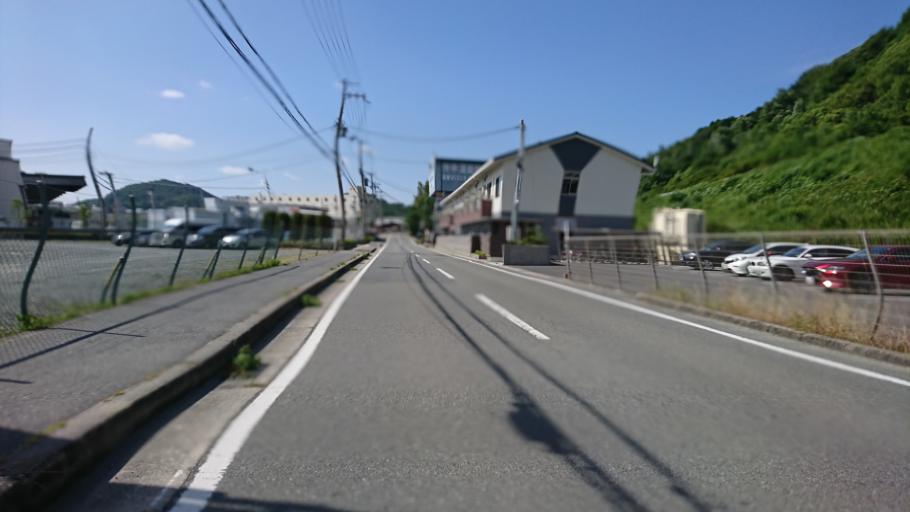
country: JP
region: Hyogo
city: Shirahamacho-usazakiminami
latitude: 34.8075
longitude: 134.7437
